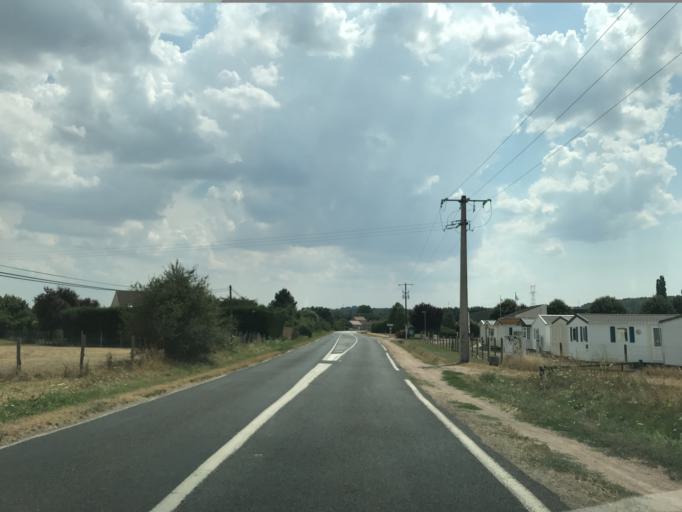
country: FR
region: Haute-Normandie
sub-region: Departement de l'Eure
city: Garennes-sur-Eure
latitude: 48.9164
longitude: 1.4443
